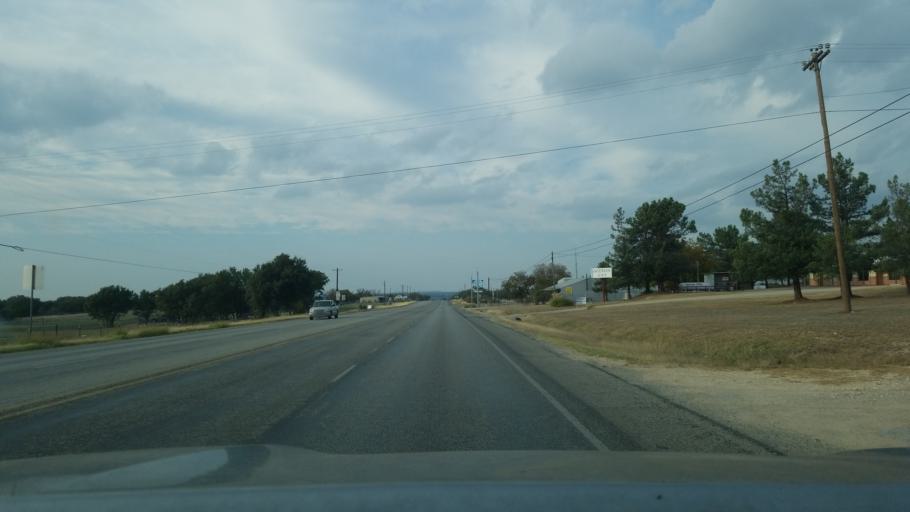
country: US
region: Texas
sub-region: Mills County
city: Goldthwaite
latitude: 31.4830
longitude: -98.5713
